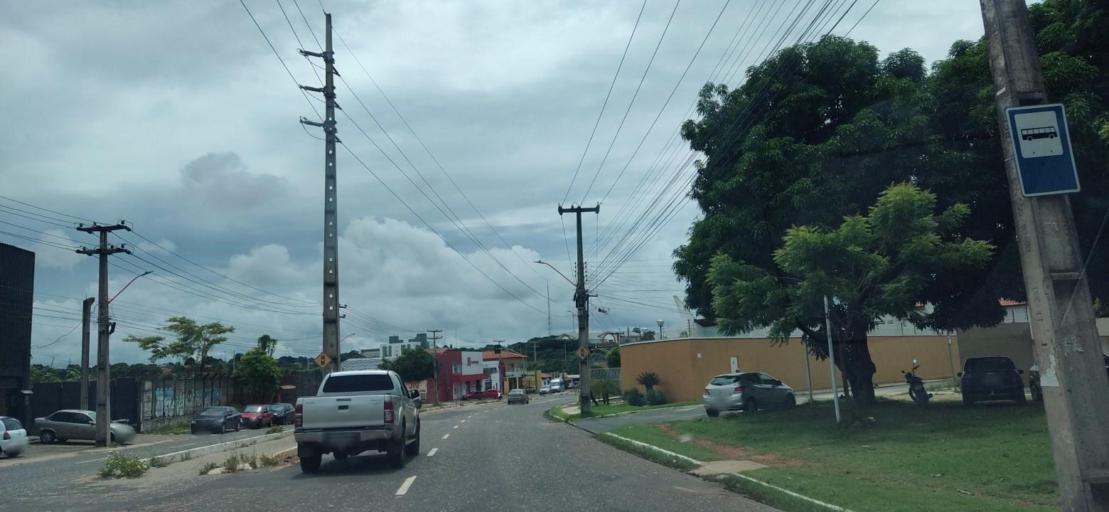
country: BR
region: Piaui
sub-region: Teresina
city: Teresina
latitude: -5.0605
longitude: -42.7555
